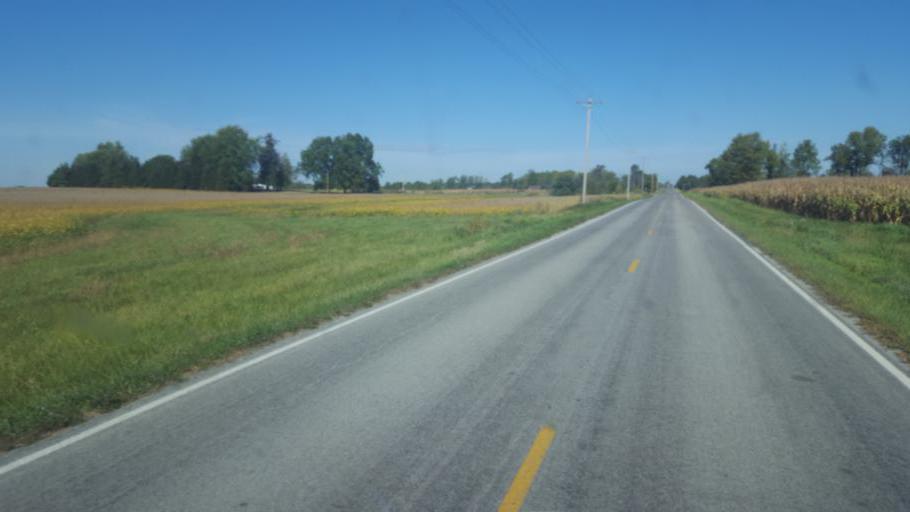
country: US
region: Ohio
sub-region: Wyandot County
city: Upper Sandusky
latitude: 40.8511
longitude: -83.1699
